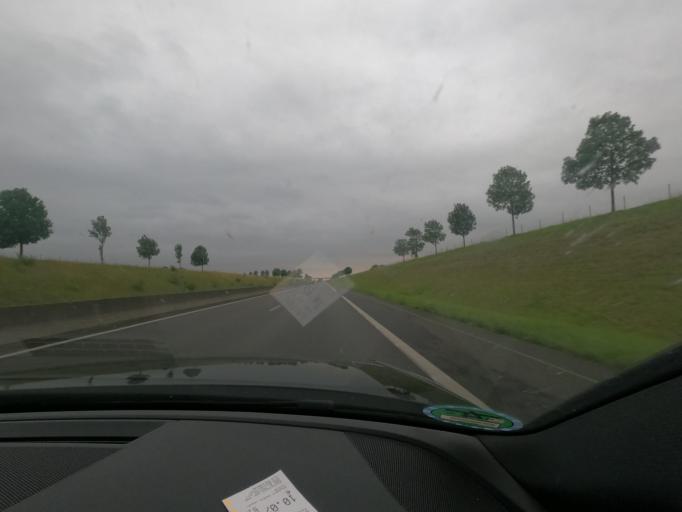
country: FR
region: Picardie
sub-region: Departement de la Somme
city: Harbonnieres
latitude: 49.8581
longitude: 2.6530
